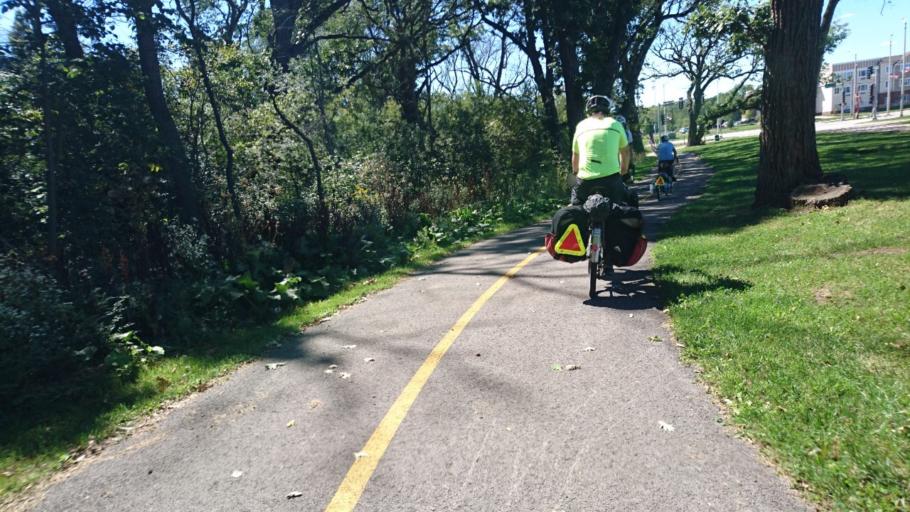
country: US
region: Illinois
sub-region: Cook County
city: Chicago Heights
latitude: 41.5105
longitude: -87.6404
